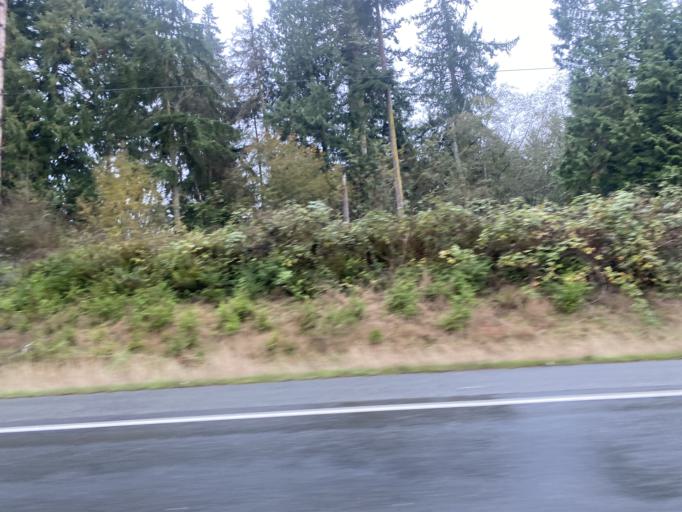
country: US
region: Washington
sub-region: Island County
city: Freeland
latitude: 48.0222
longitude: -122.5575
